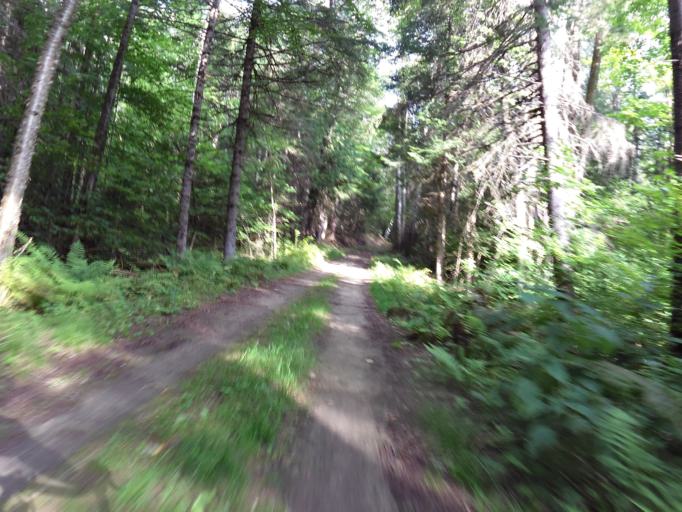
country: CA
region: Quebec
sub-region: Outaouais
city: Wakefield
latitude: 45.6272
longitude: -75.9731
